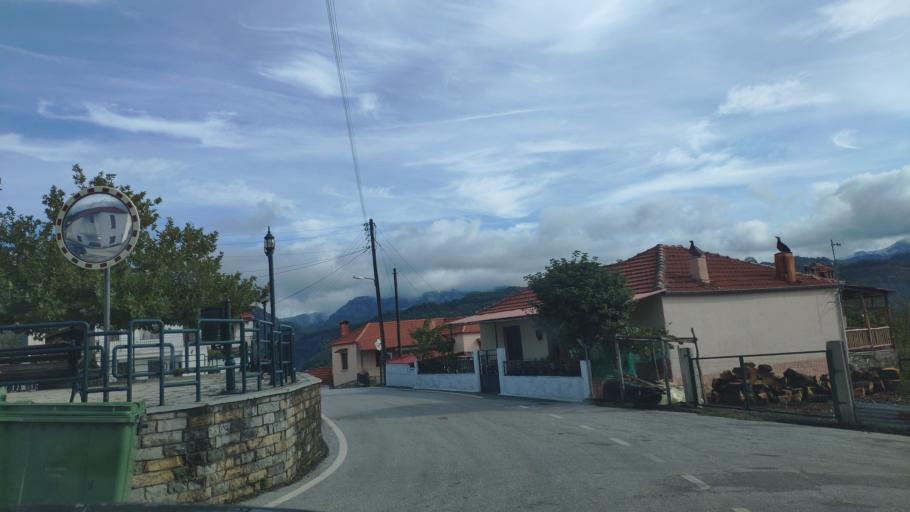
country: GR
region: West Macedonia
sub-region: Nomos Kastorias
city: Nestorio
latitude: 40.2745
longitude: 20.9755
